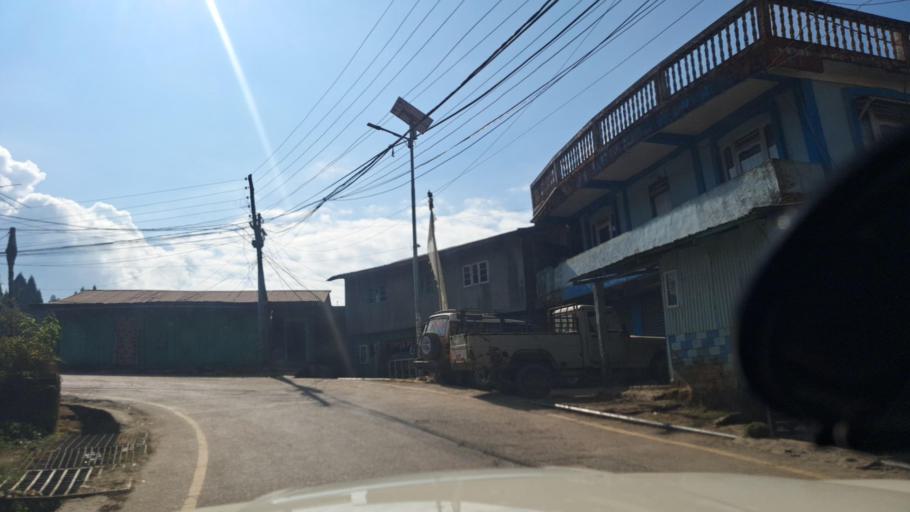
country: IN
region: West Bengal
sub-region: Darjiling
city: Mirik
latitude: 26.9495
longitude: 88.1182
